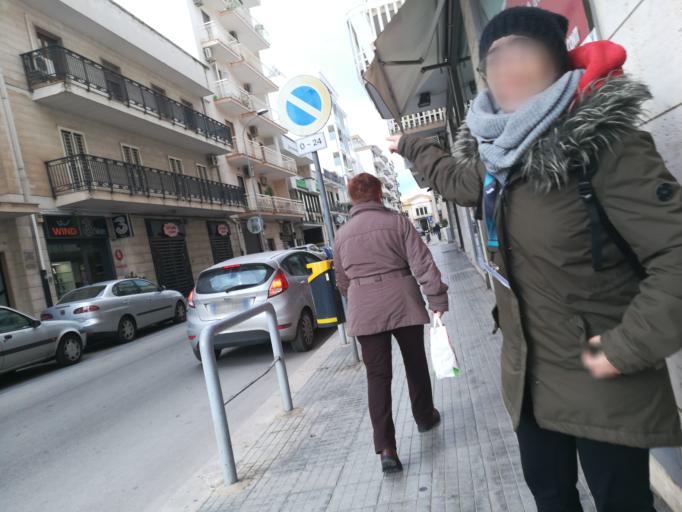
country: IT
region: Apulia
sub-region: Provincia di Bari
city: Bitonto
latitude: 41.1117
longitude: 16.6933
